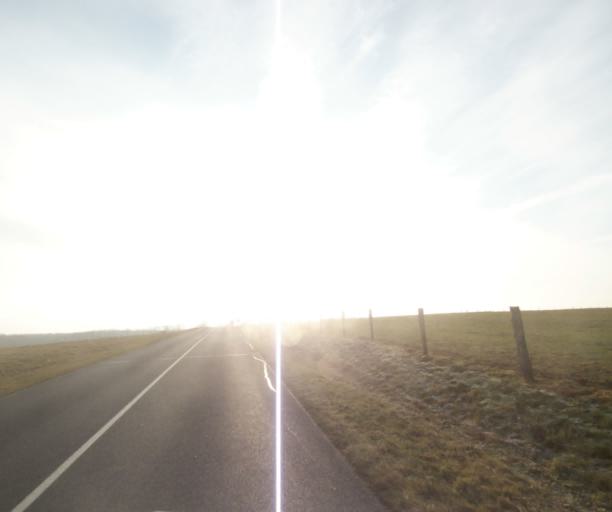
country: FR
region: Champagne-Ardenne
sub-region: Departement de la Marne
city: Sermaize-les-Bains
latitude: 48.7321
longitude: 4.9310
